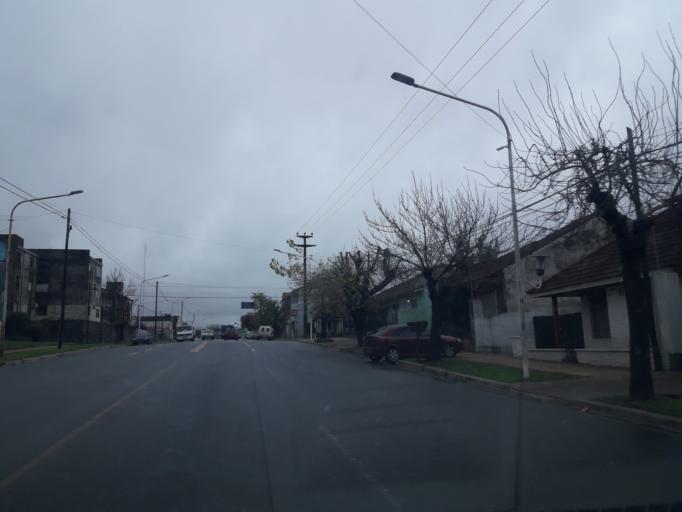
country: AR
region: Buenos Aires
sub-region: Partido de Tandil
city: Tandil
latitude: -37.3182
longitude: -59.1517
